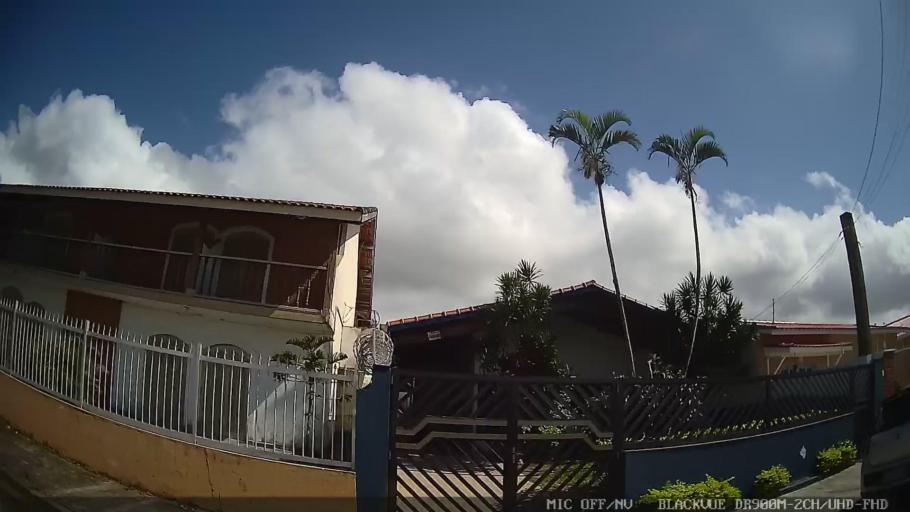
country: BR
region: Sao Paulo
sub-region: Peruibe
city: Peruibe
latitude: -24.3203
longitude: -46.9923
